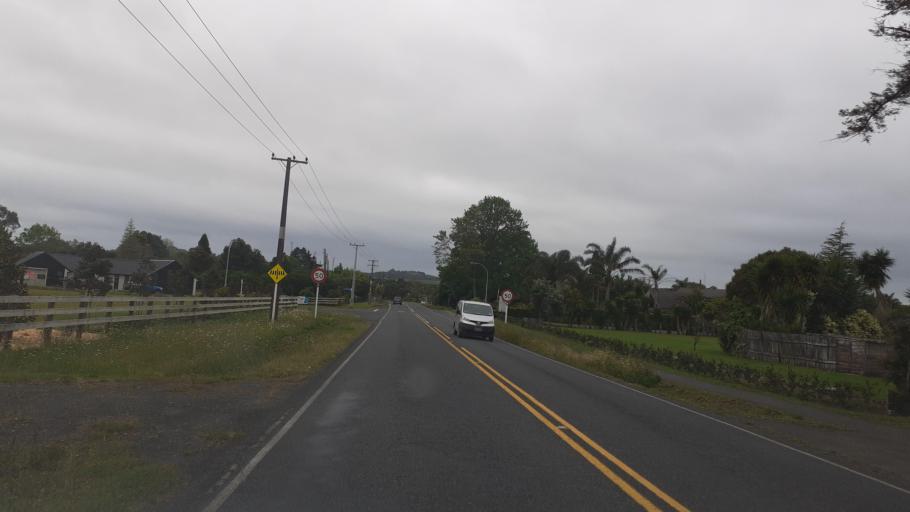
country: NZ
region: Northland
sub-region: Far North District
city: Kerikeri
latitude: -35.2086
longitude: 173.9640
